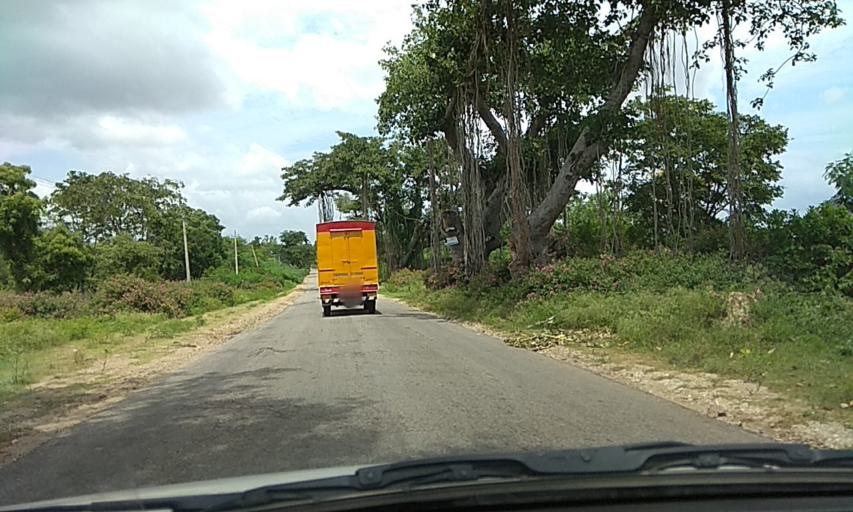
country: IN
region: Karnataka
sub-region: Chamrajnagar
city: Gundlupet
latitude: 11.8128
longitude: 76.7684
